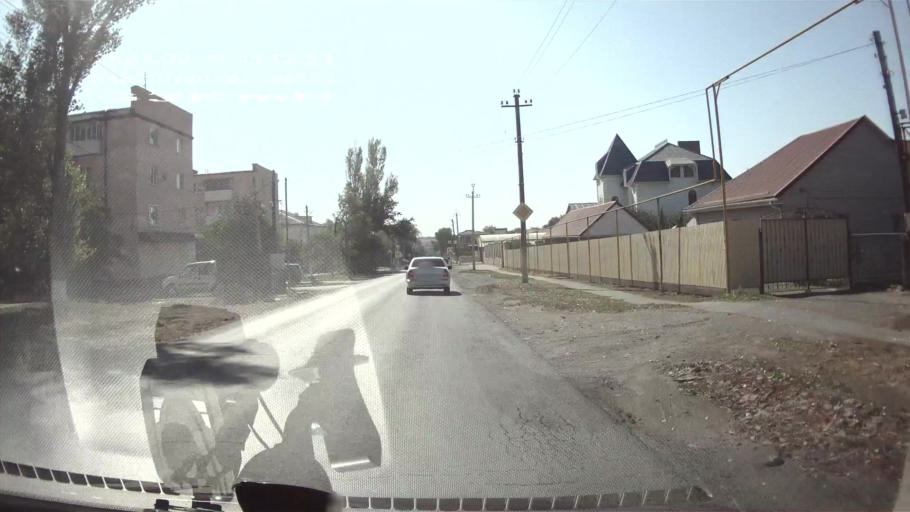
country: RU
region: Rostov
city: Gigant
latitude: 46.5115
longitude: 41.3396
